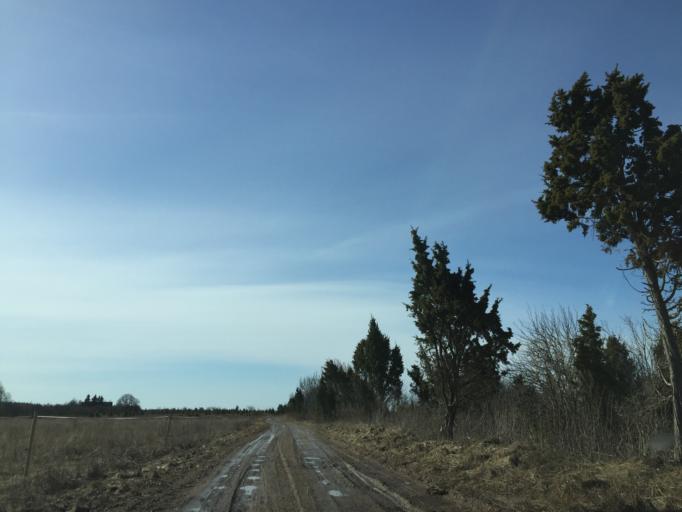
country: EE
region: Laeaene
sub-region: Haapsalu linn
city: Haapsalu
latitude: 58.6505
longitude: 23.5135
